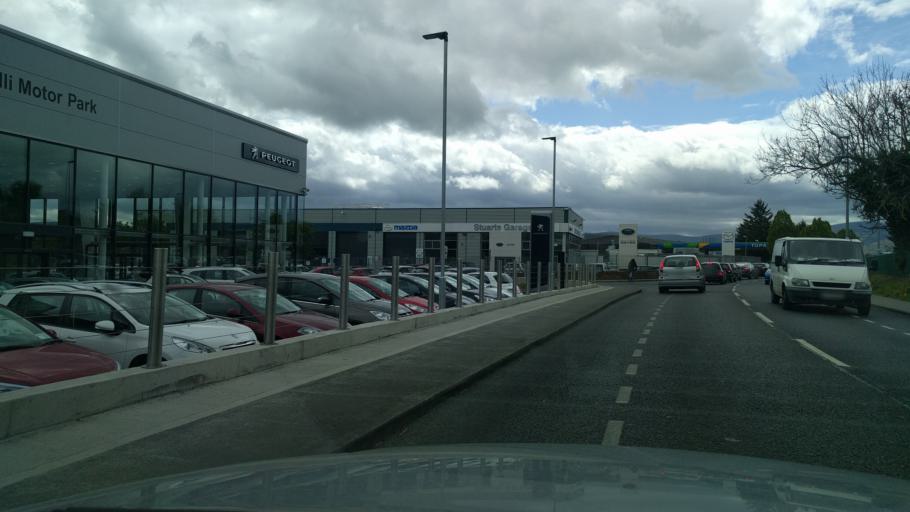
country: IE
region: Leinster
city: Firhouse
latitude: 53.2970
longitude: -6.3542
